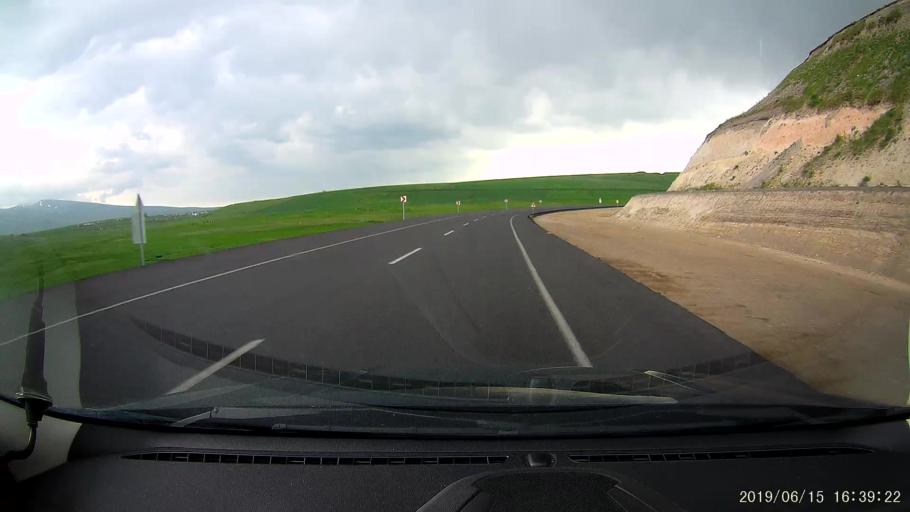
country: TR
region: Ardahan
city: Haskoy
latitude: 40.9835
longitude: 42.8970
